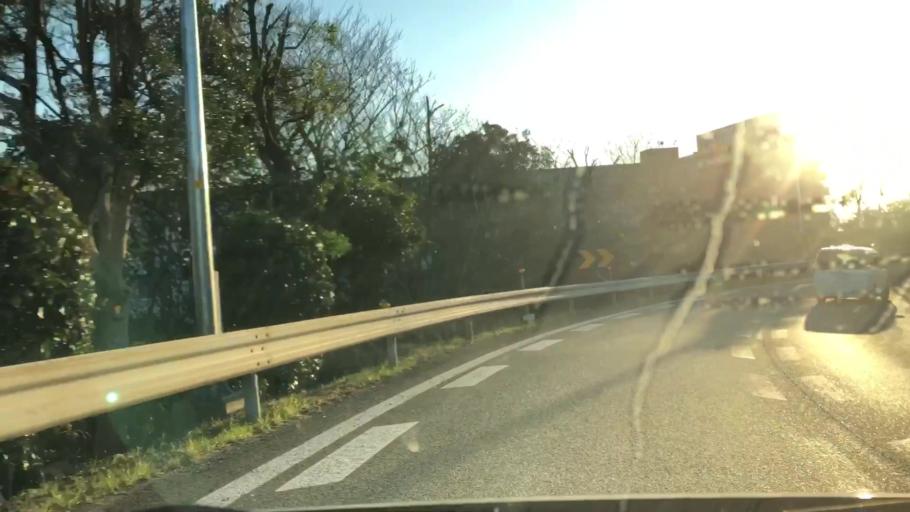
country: JP
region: Fukuoka
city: Umi
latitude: 33.6285
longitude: 130.4841
